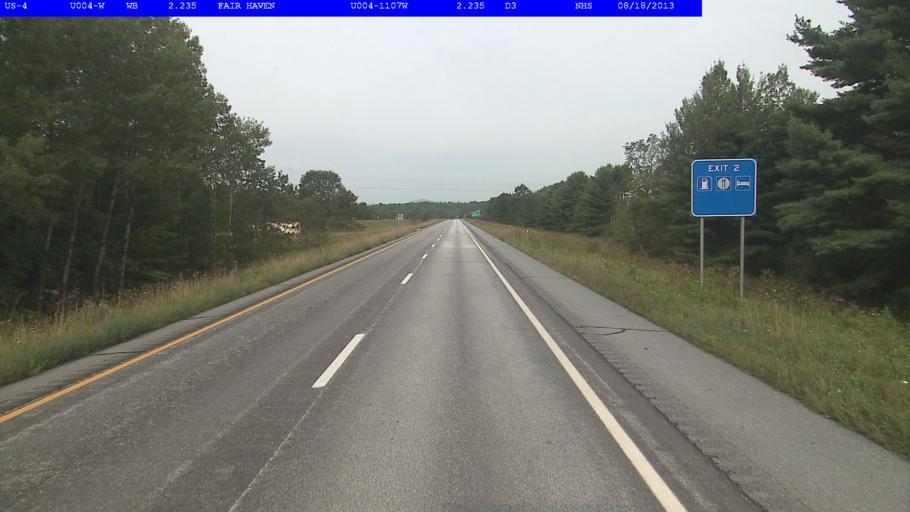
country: US
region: Vermont
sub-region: Rutland County
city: Fair Haven
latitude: 43.6060
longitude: -73.2668
